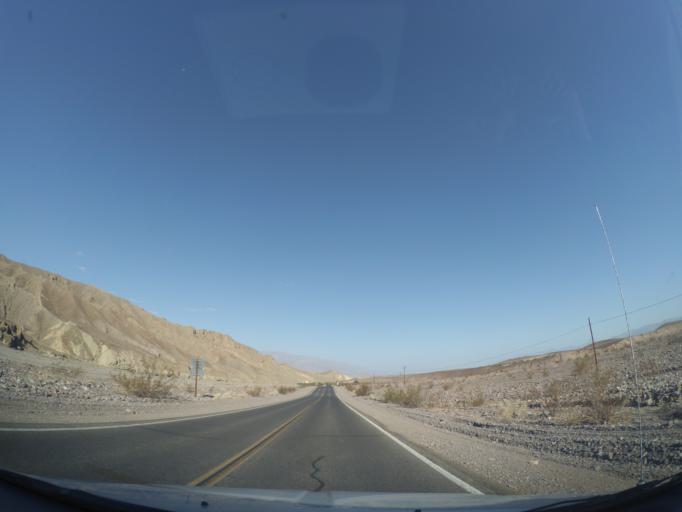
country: US
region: Nevada
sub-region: Nye County
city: Beatty
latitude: 36.4383
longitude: -116.8258
